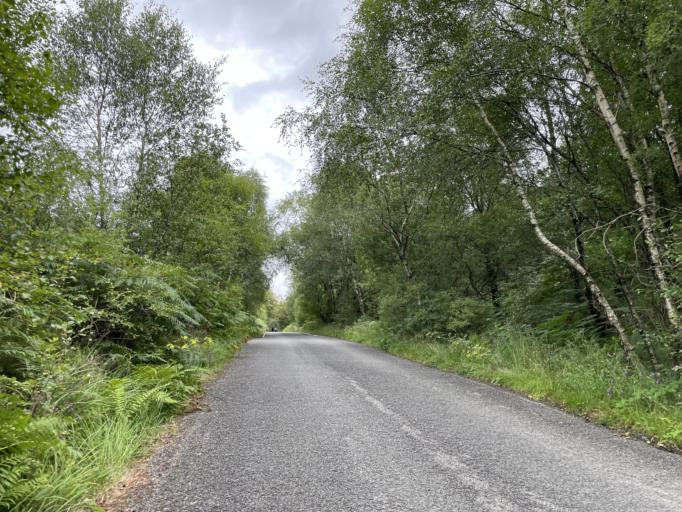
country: GB
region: Scotland
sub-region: Dumfries and Galloway
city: Newton Stewart
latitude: 55.0907
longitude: -4.4895
